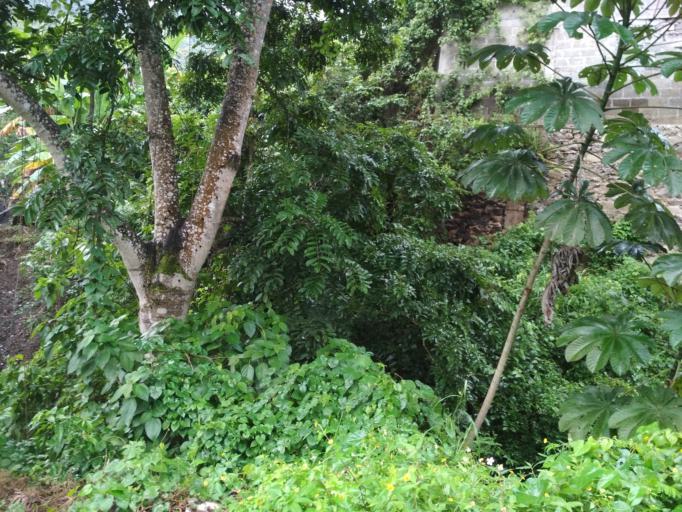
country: MX
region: Veracruz
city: San Andres Tuxtla
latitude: 18.4519
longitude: -95.1977
